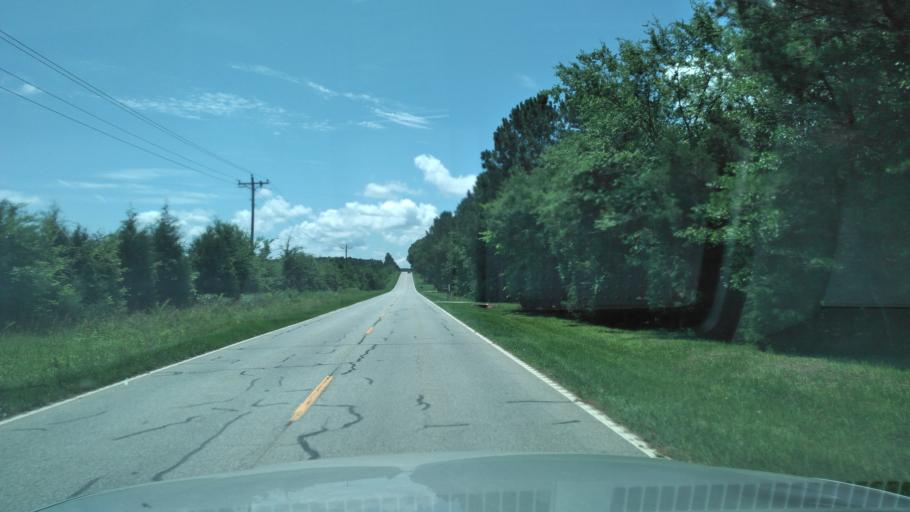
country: US
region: South Carolina
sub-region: Greenwood County
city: Ninety Six
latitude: 34.3294
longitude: -82.0554
